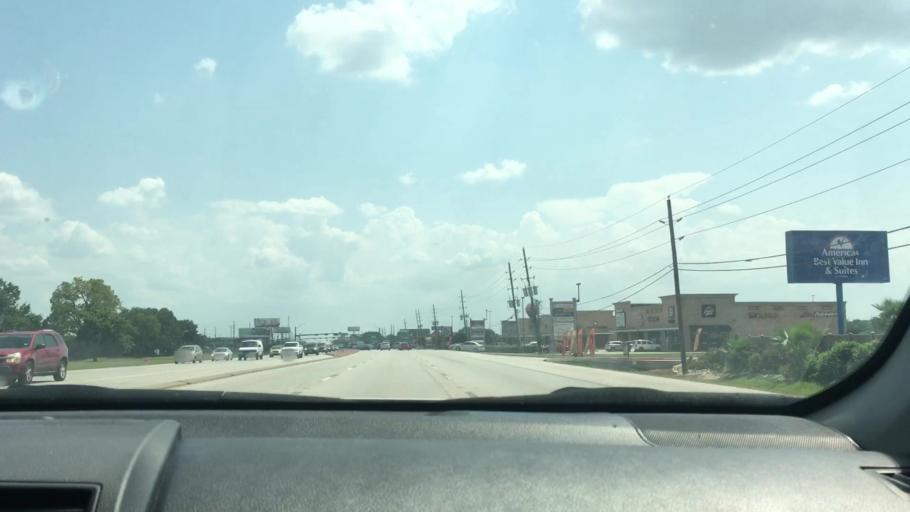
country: US
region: Texas
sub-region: Fort Bend County
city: Mission Bend
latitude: 29.7236
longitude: -95.6441
